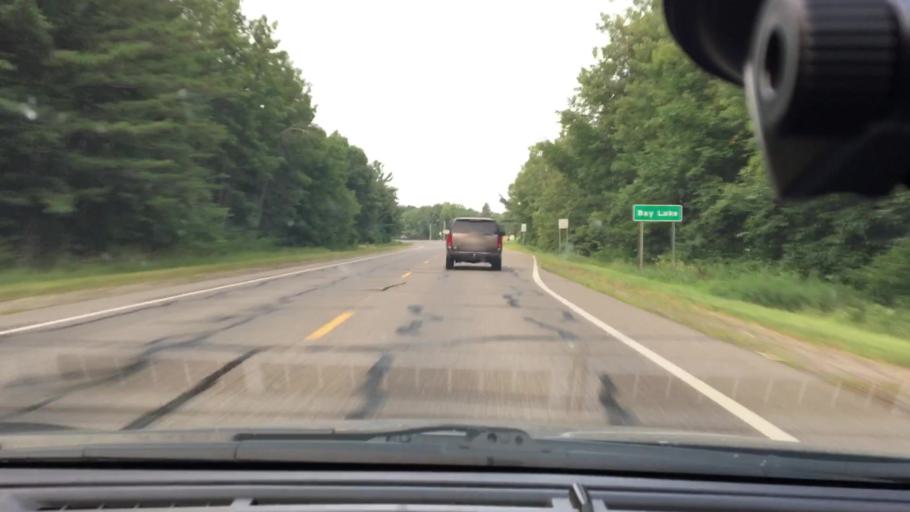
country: US
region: Minnesota
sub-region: Crow Wing County
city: Crosby
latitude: 46.4070
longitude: -93.8767
